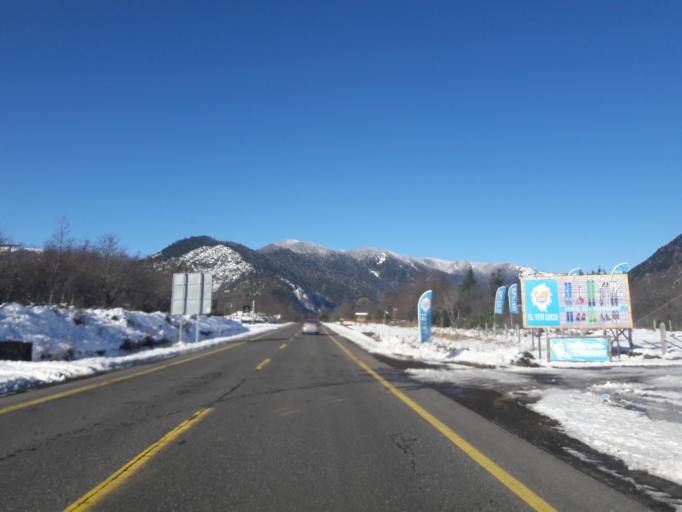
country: CL
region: Araucania
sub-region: Provincia de Cautin
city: Vilcun
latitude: -38.4751
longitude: -71.5504
